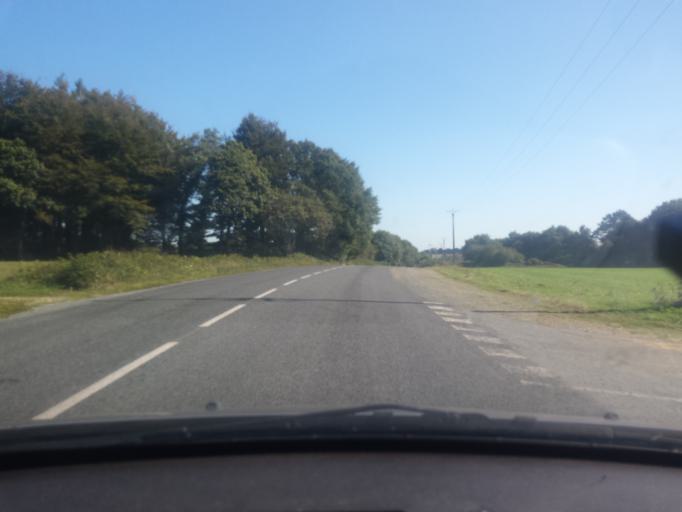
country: FR
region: Brittany
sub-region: Departement des Cotes-d'Armor
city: Gouarec
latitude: 48.1764
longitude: -3.1668
